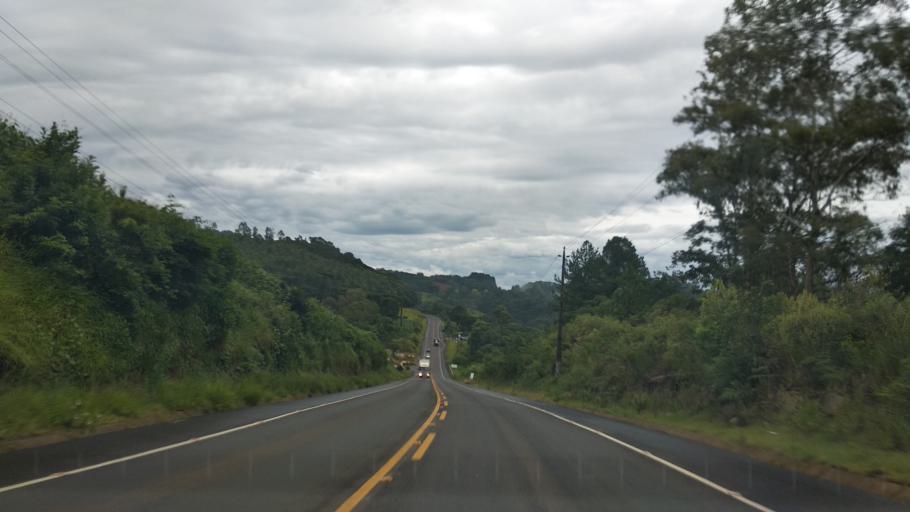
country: BR
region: Santa Catarina
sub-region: Videira
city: Videira
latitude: -27.0469
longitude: -51.1642
